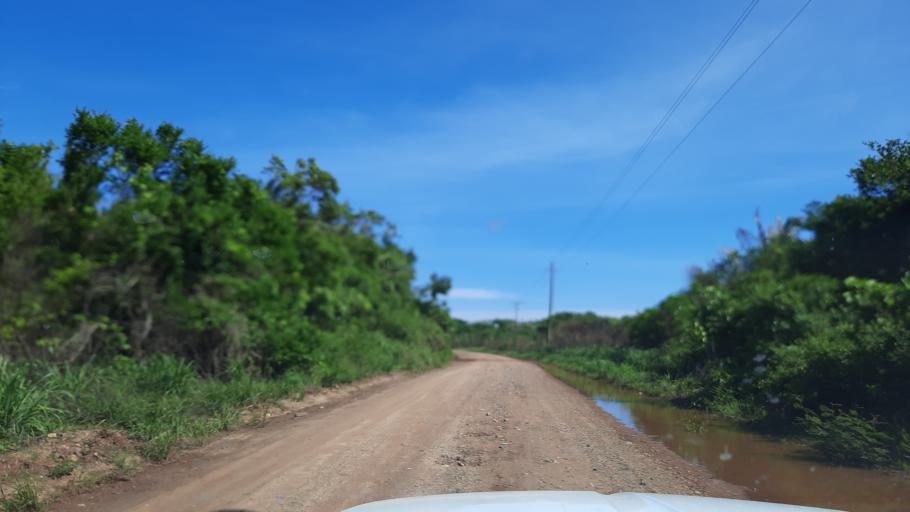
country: BZ
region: Stann Creek
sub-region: Dangriga
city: Dangriga
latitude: 17.1608
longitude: -88.3287
